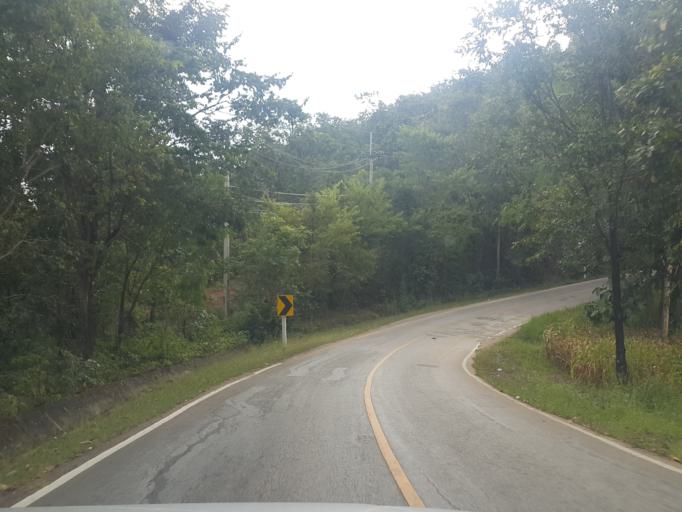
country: TH
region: Chiang Mai
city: Mae Chaem
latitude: 18.5108
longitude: 98.4153
